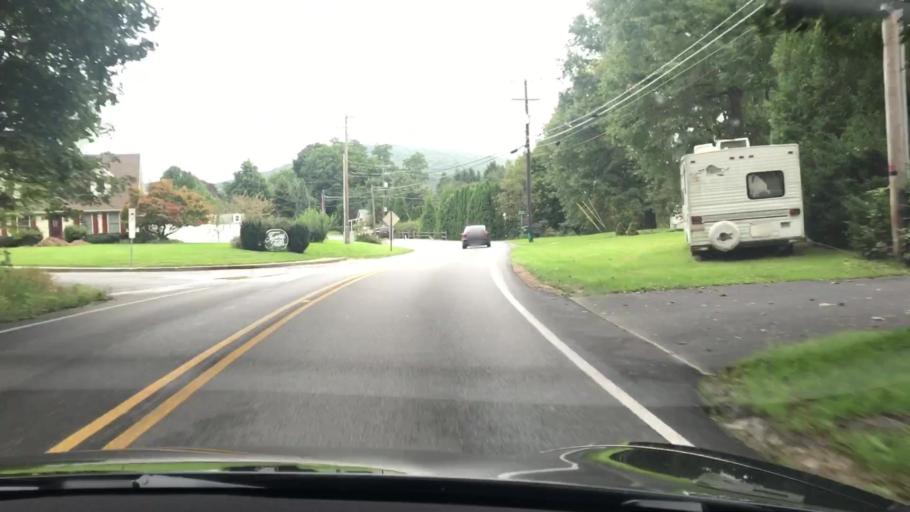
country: US
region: Pennsylvania
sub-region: York County
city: Dillsburg
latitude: 40.1075
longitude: -77.0540
